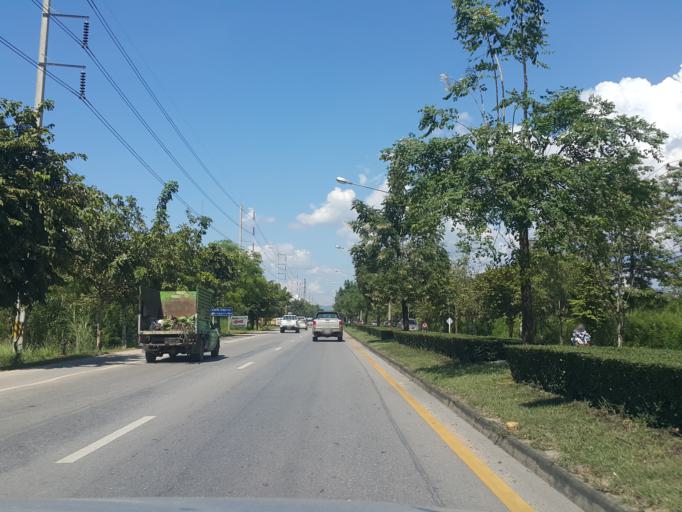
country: TH
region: Chiang Mai
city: San Sai
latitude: 18.8504
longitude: 99.0139
